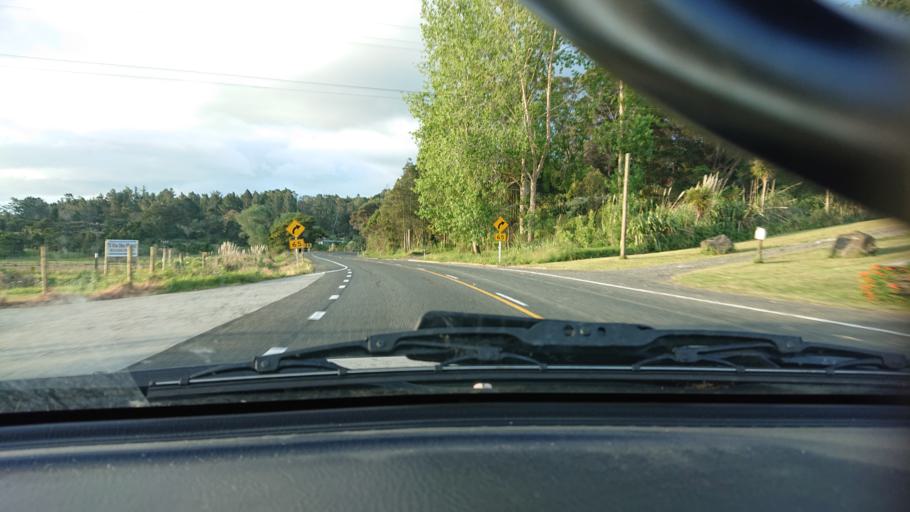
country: NZ
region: Auckland
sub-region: Auckland
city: Parakai
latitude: -36.5315
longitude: 174.4553
